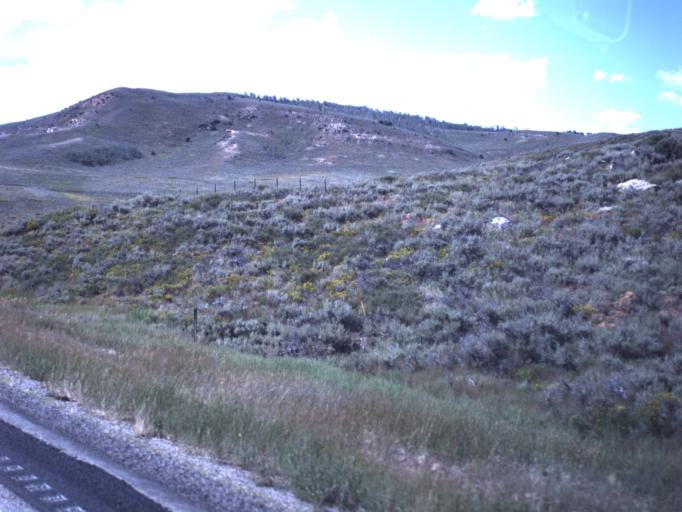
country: US
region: Utah
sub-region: Wasatch County
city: Heber
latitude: 40.1938
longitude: -111.0870
